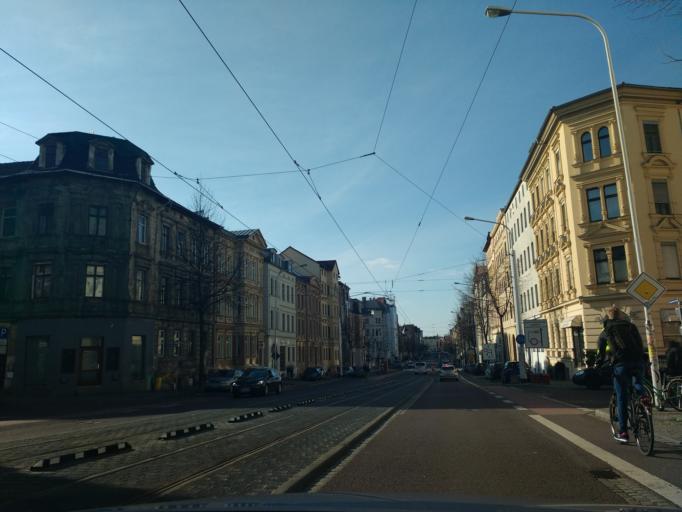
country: DE
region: Saxony-Anhalt
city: Halle (Saale)
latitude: 51.4925
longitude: 11.9724
